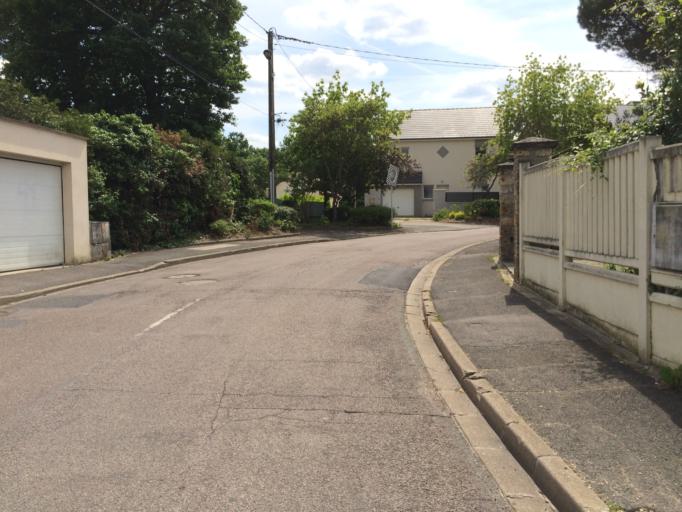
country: FR
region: Ile-de-France
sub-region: Departement de l'Essonne
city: Palaiseau
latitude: 48.7242
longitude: 2.2348
